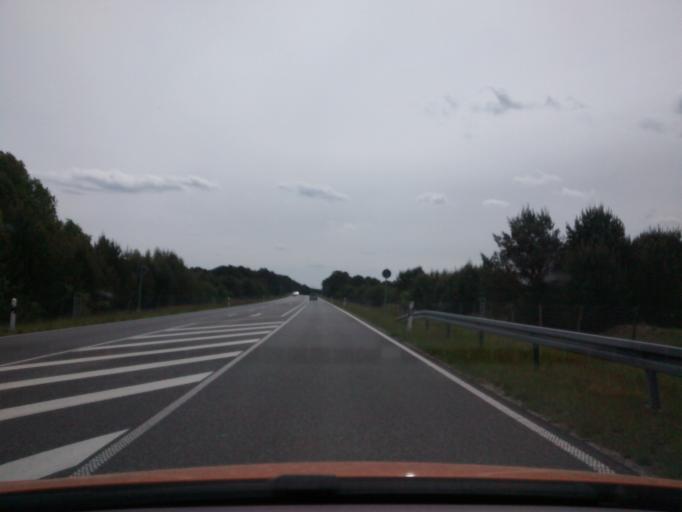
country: DE
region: Brandenburg
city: Luckenwalde
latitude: 52.0879
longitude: 13.1234
